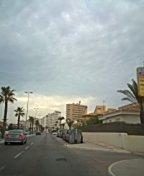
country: ES
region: Murcia
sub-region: Murcia
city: La Manga del Mar Menor
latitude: 37.7196
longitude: -0.7415
